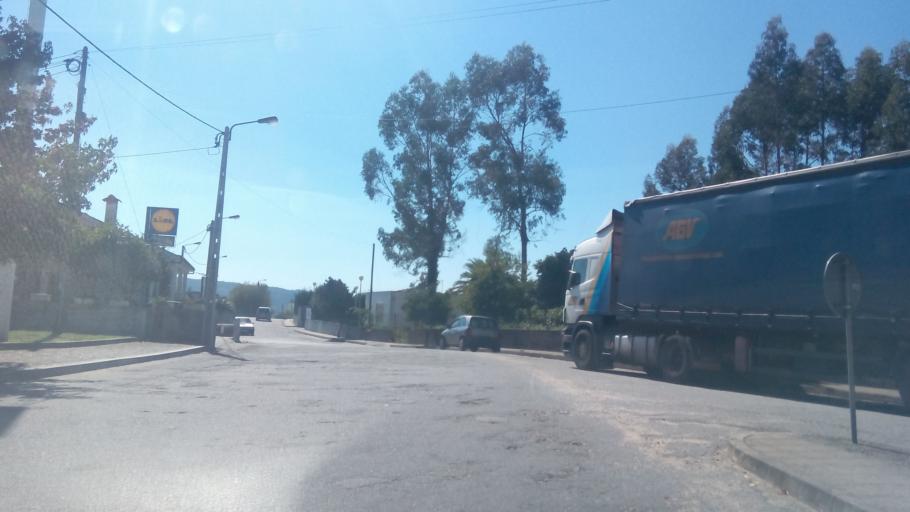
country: PT
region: Porto
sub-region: Paredes
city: Casteloes de Cepeda
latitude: 41.1999
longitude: -8.3342
